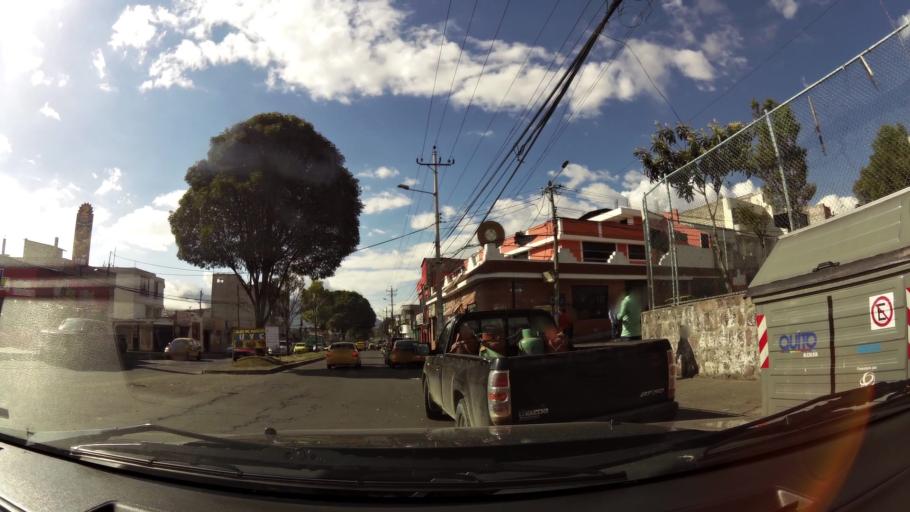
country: EC
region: Pichincha
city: Quito
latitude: -0.1188
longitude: -78.4838
